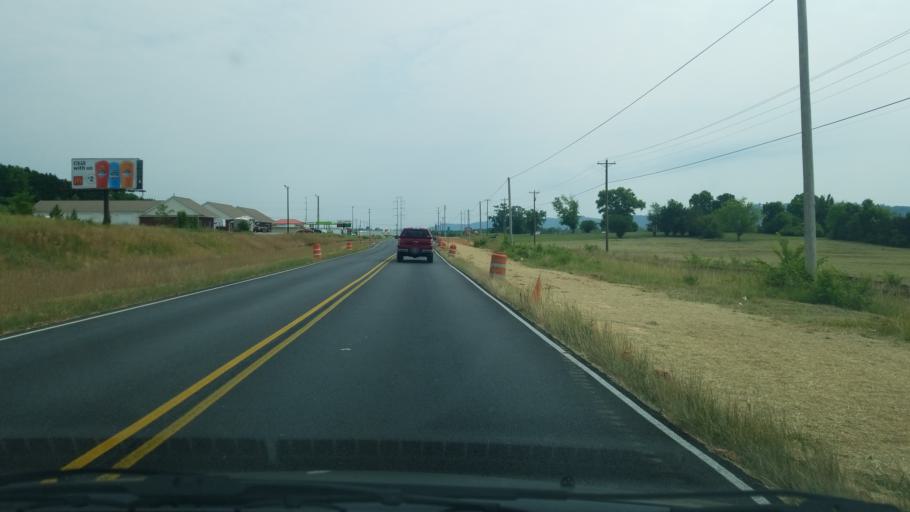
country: US
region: Georgia
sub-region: Catoosa County
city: Ringgold
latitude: 34.8929
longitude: -85.1326
